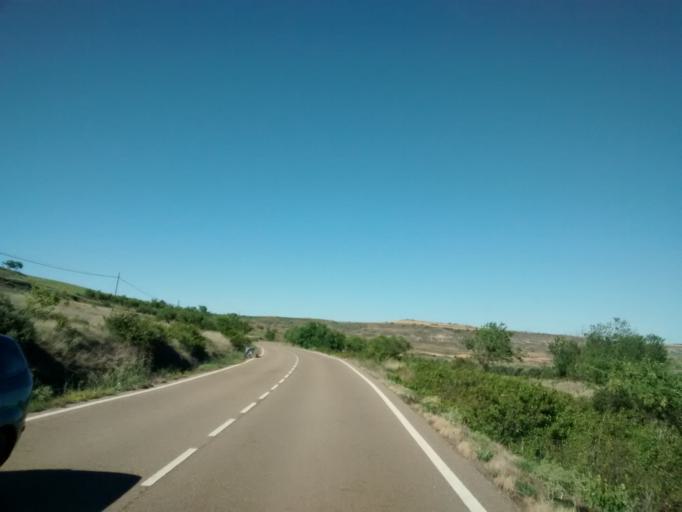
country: ES
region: Aragon
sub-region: Provincia de Zaragoza
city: Trasmoz
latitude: 41.8344
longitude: -1.7141
